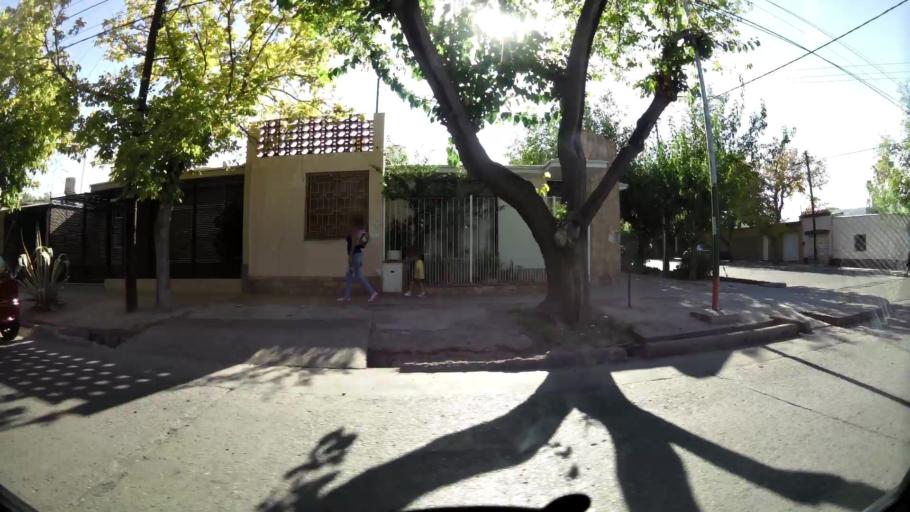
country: AR
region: Mendoza
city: Mendoza
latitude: -32.9050
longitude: -68.8250
